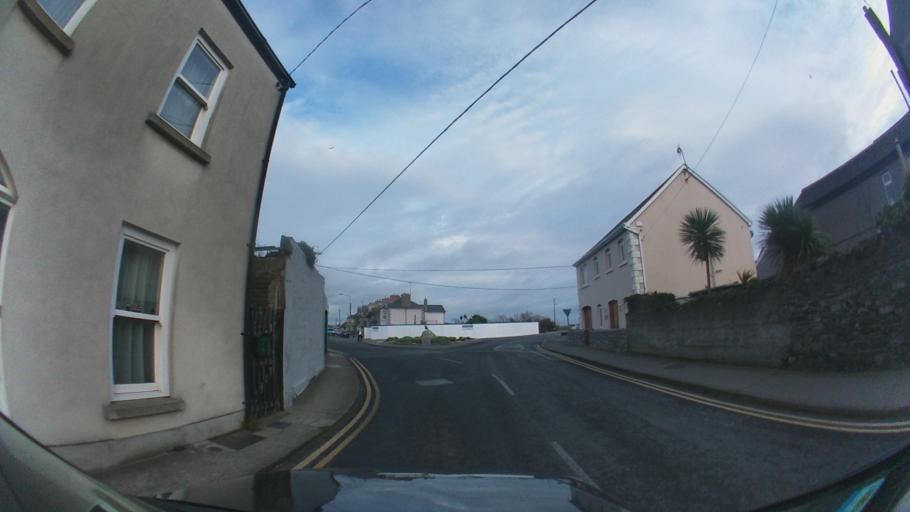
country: IE
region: Leinster
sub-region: Fingal County
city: Skerries
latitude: 53.5813
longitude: -6.1075
